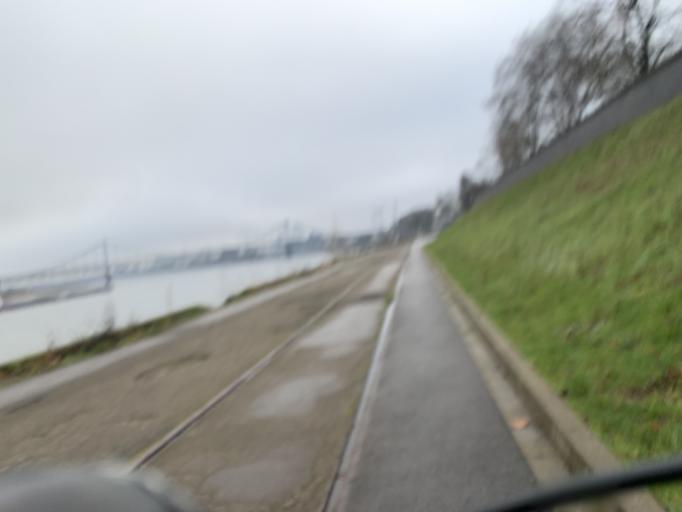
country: DE
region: North Rhine-Westphalia
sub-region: Regierungsbezirk Dusseldorf
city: Krefeld
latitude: 51.3550
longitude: 6.6522
